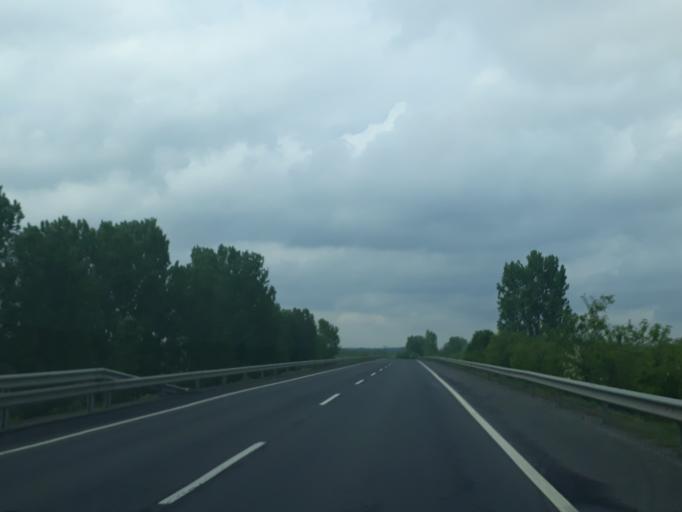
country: HU
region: Szabolcs-Szatmar-Bereg
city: Ajak
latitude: 48.1836
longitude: 22.0421
